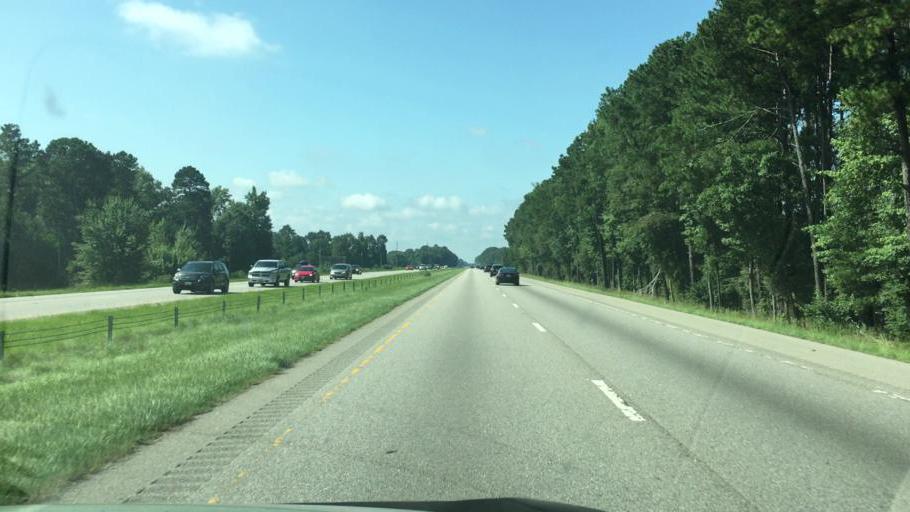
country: US
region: North Carolina
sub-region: Cumberland County
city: Hope Mills
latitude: 34.8992
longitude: -78.9585
